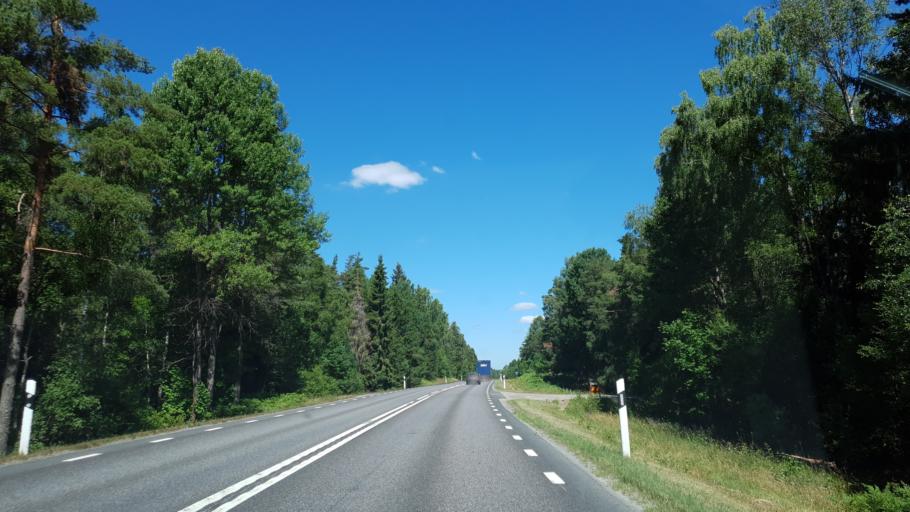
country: SE
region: Joenkoeping
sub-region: Varnamo Kommun
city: Rydaholm
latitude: 57.0086
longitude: 14.2619
